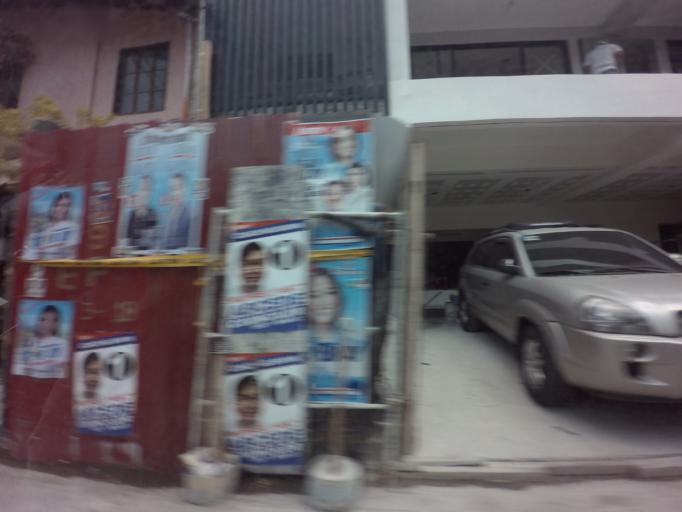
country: PH
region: Metro Manila
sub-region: Makati City
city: Makati City
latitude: 14.5657
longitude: 121.0336
